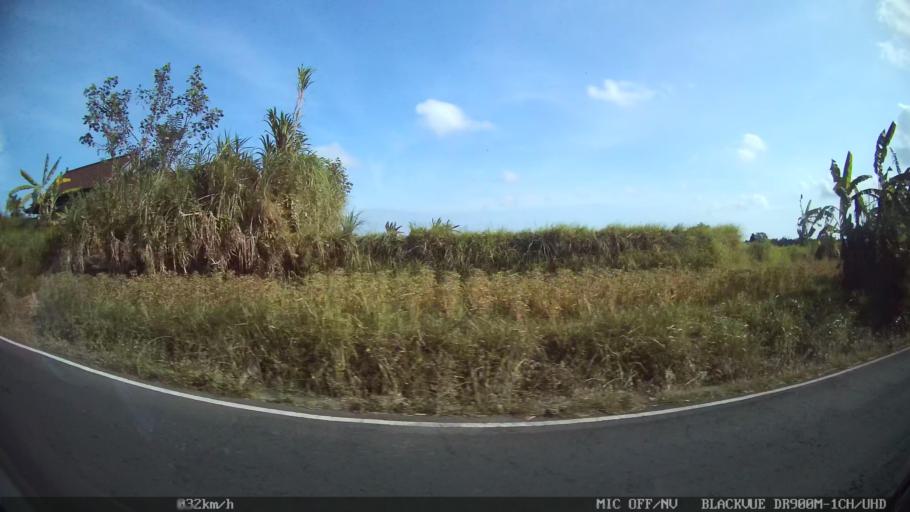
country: ID
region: Bali
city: Banjar Parekan
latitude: -8.5795
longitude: 115.2226
